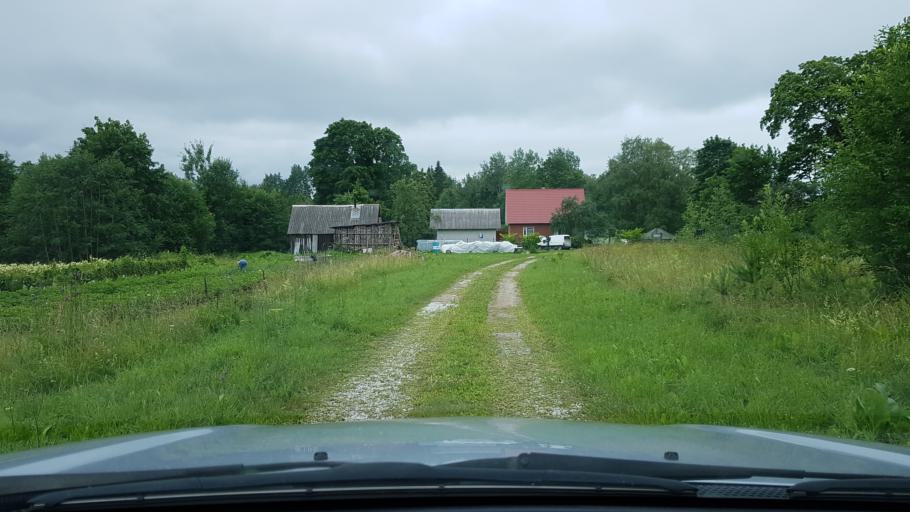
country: EE
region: Ida-Virumaa
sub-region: Narva-Joesuu linn
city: Narva-Joesuu
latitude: 59.3601
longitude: 28.0397
